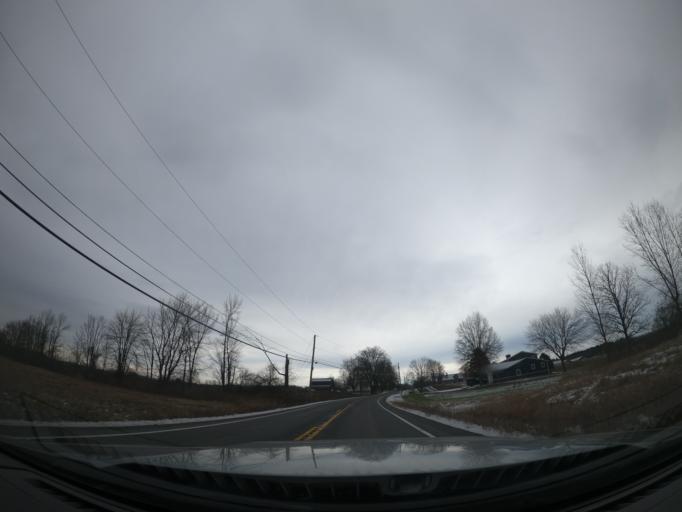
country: US
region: New York
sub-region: Onondaga County
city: Minoa
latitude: 43.1135
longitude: -76.0200
